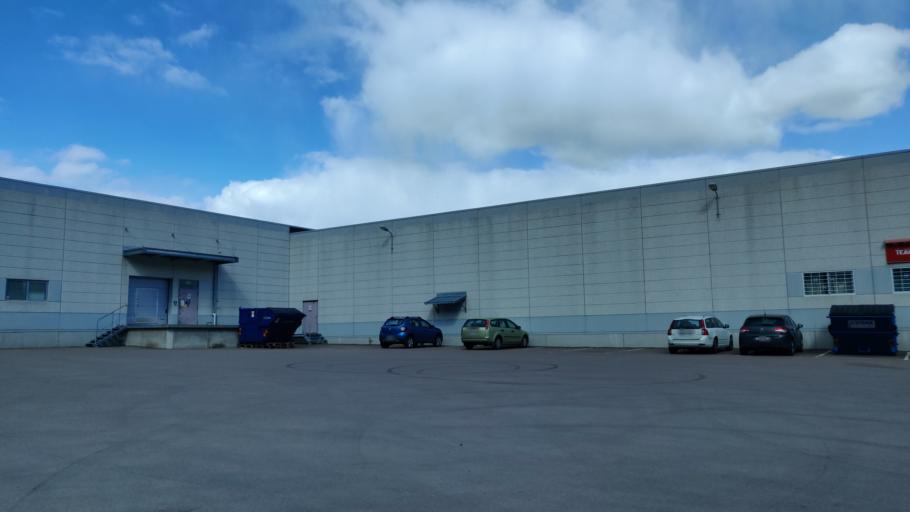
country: SE
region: Vaermland
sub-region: Hammaro Kommun
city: Skoghall
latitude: 59.3747
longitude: 13.4386
